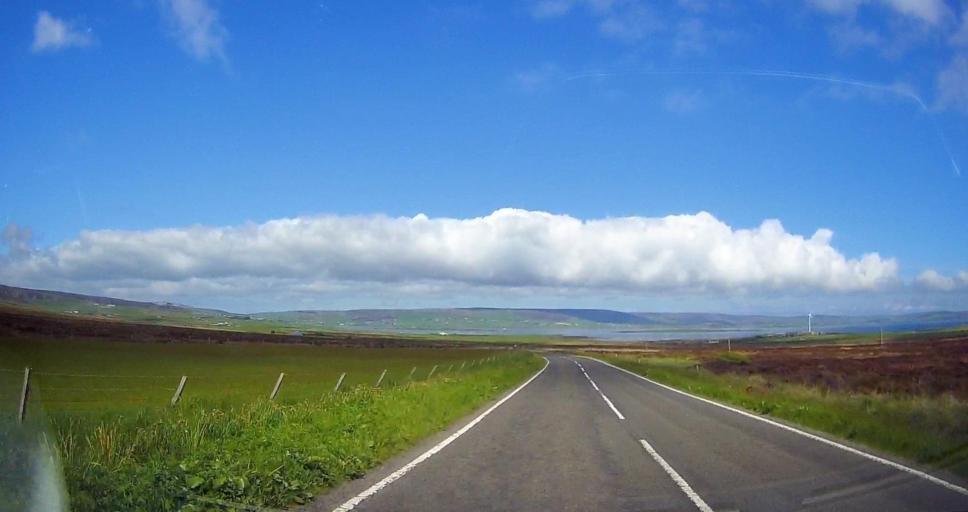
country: GB
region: Scotland
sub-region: Orkney Islands
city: Orkney
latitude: 58.9846
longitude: -3.0453
